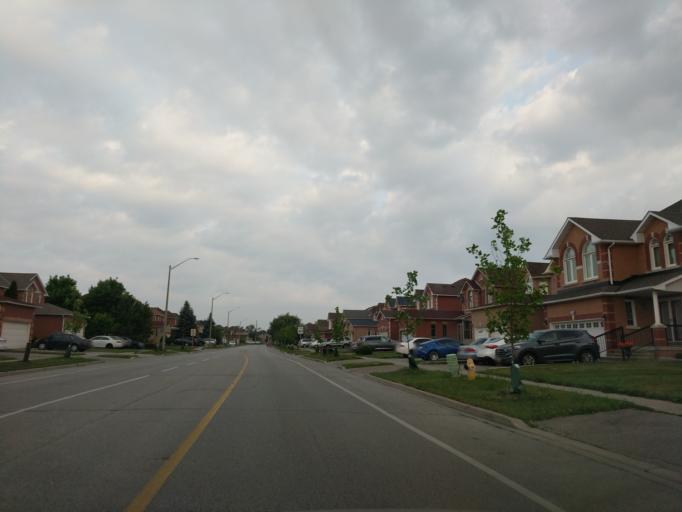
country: CA
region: Ontario
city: Markham
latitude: 43.8472
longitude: -79.2754
